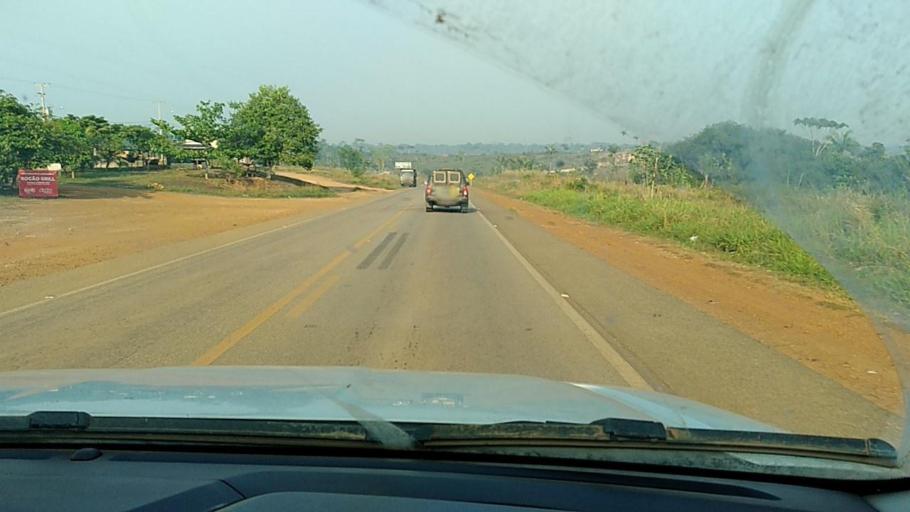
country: BR
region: Rondonia
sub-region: Porto Velho
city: Porto Velho
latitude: -8.7416
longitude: -63.9451
